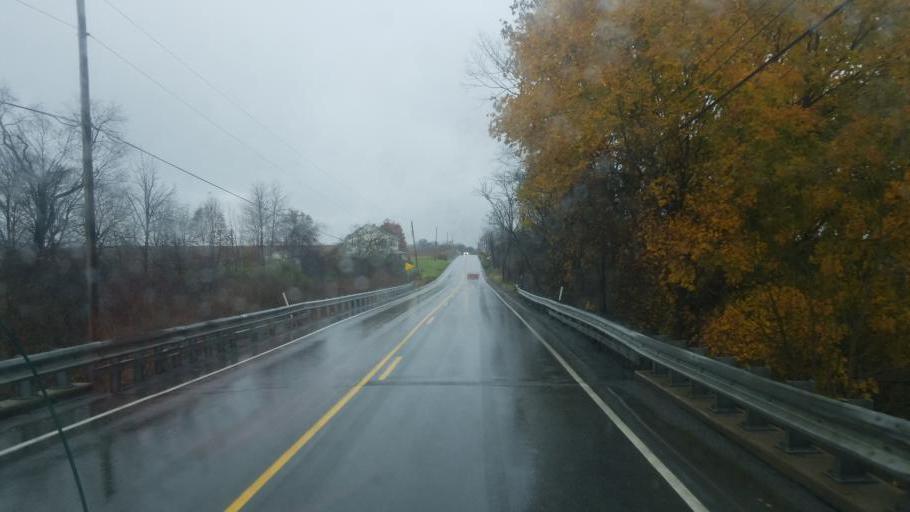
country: US
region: Pennsylvania
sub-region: Clinton County
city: Mill Hall
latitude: 41.0981
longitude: -77.5209
